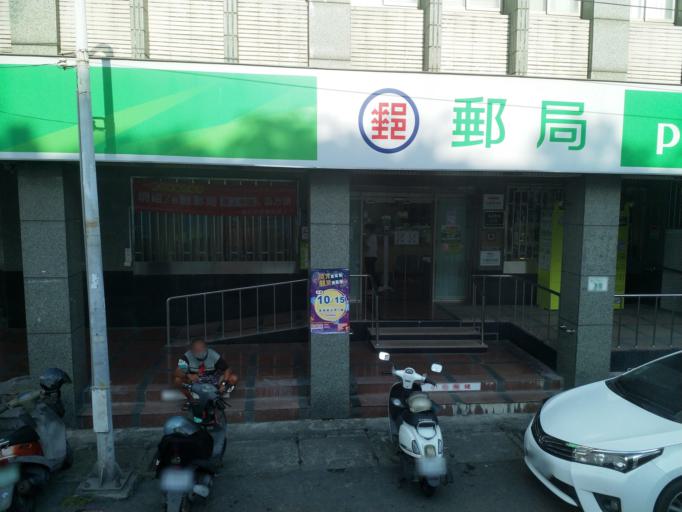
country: TW
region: Taiwan
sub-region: Pingtung
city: Pingtung
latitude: 22.9007
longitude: 120.5417
